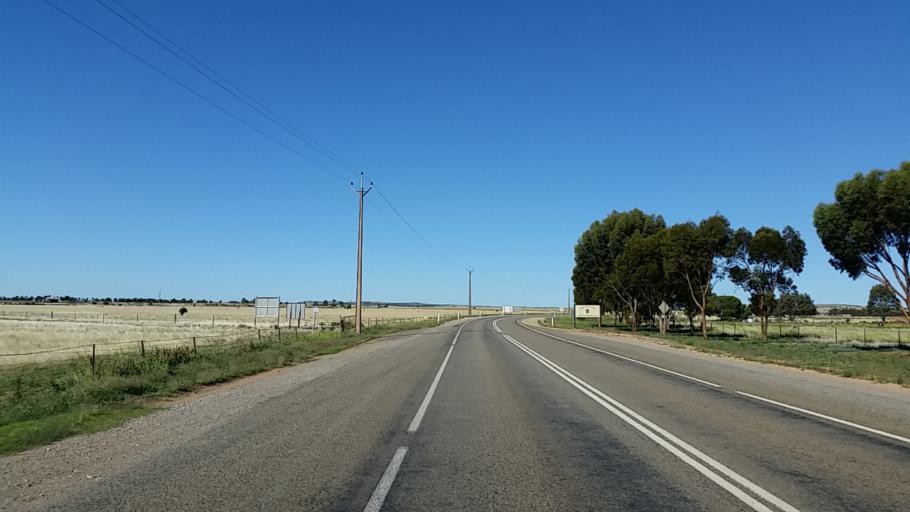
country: AU
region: South Australia
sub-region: Peterborough
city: Peterborough
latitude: -32.9715
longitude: 138.8499
